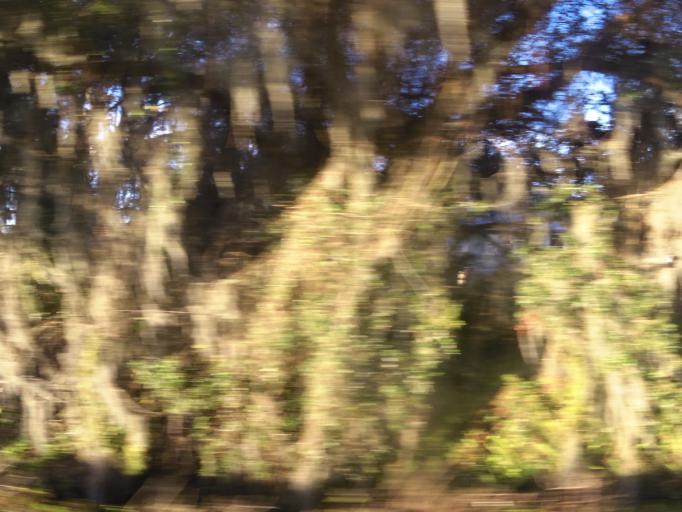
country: US
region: Florida
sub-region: Saint Johns County
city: Saint Augustine Shores
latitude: 29.7842
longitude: -81.4512
